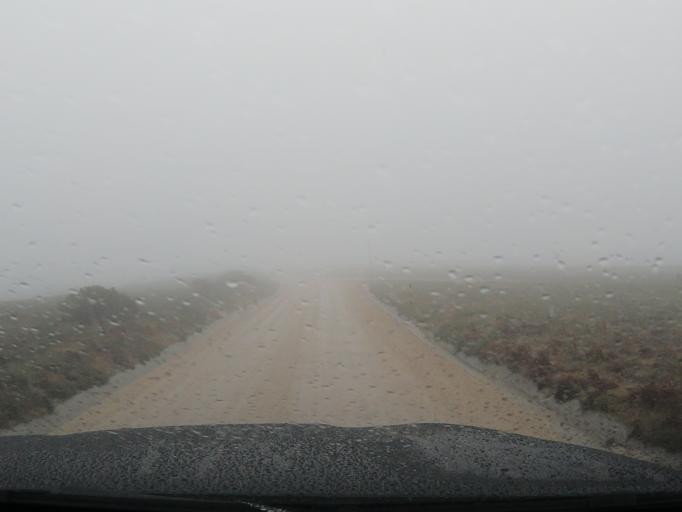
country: PT
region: Vila Real
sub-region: Vila Real
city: Vila Real
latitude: 41.3323
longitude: -7.8368
